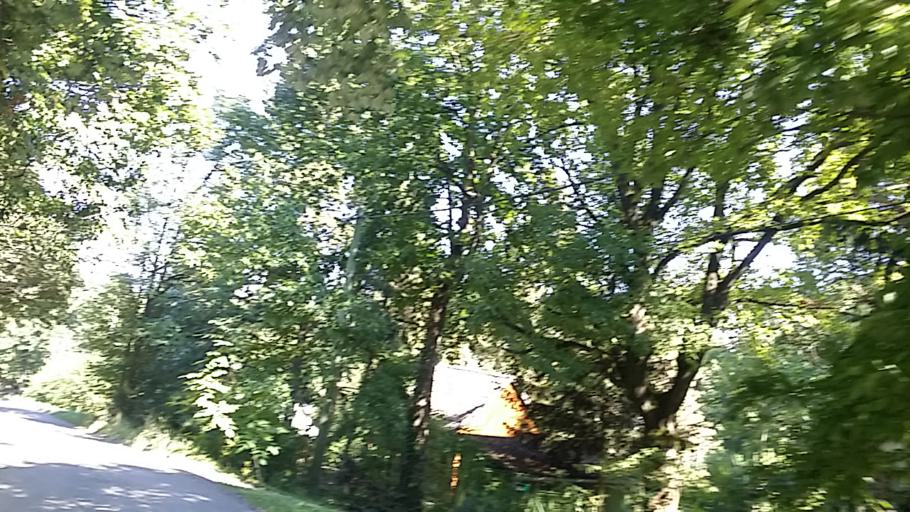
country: HU
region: Pest
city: Kismaros
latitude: 47.8401
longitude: 18.9962
